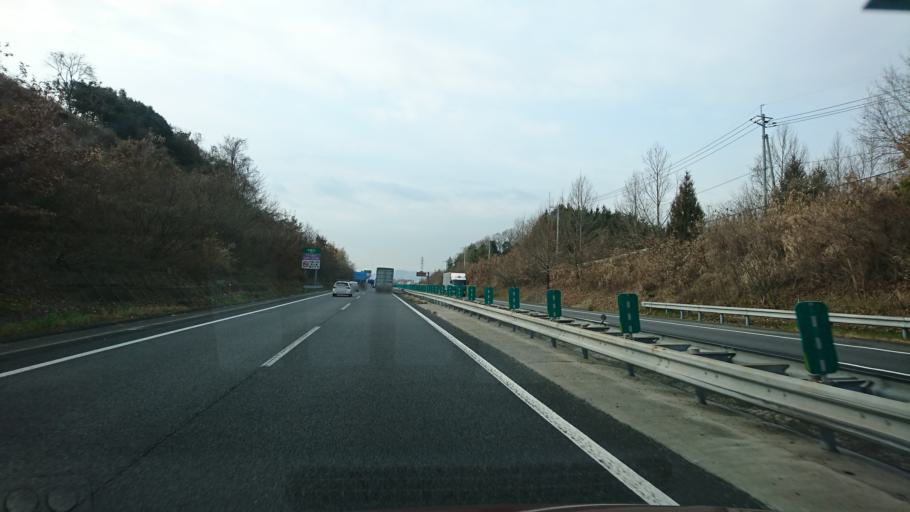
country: JP
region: Okayama
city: Okayama-shi
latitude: 34.6996
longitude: 133.8840
